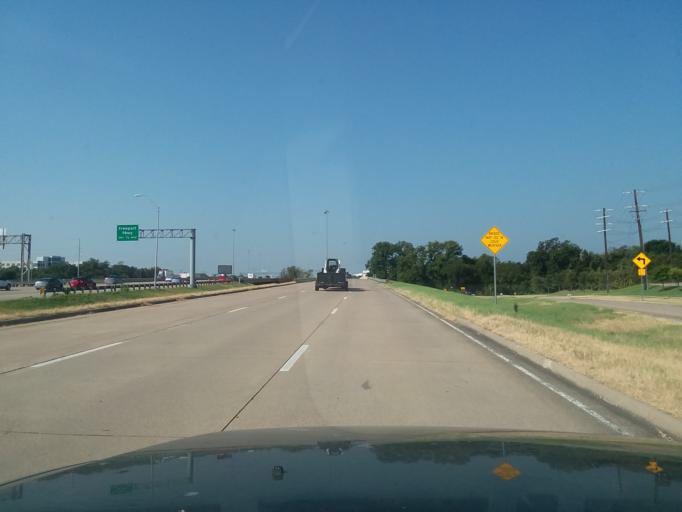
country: US
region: Texas
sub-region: Dallas County
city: Coppell
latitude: 32.9888
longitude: -97.0118
